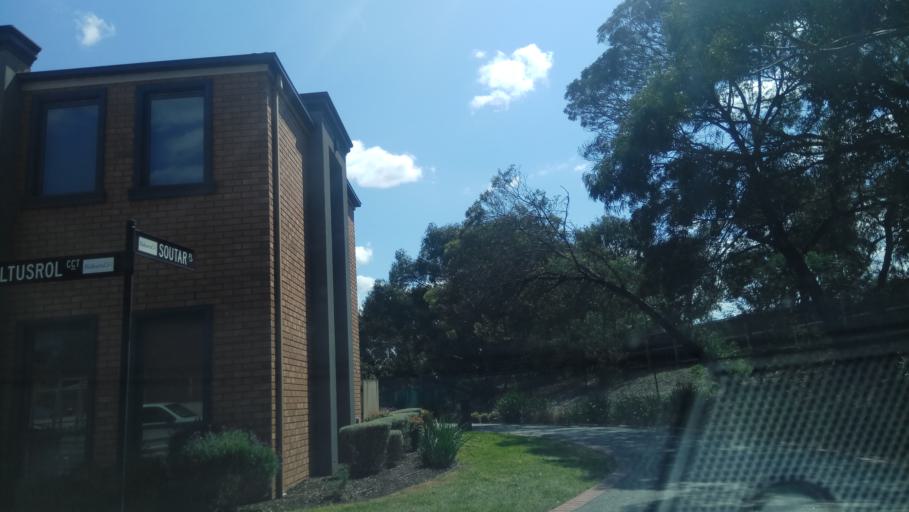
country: AU
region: Victoria
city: Heatherton
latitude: -37.9606
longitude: 145.0844
